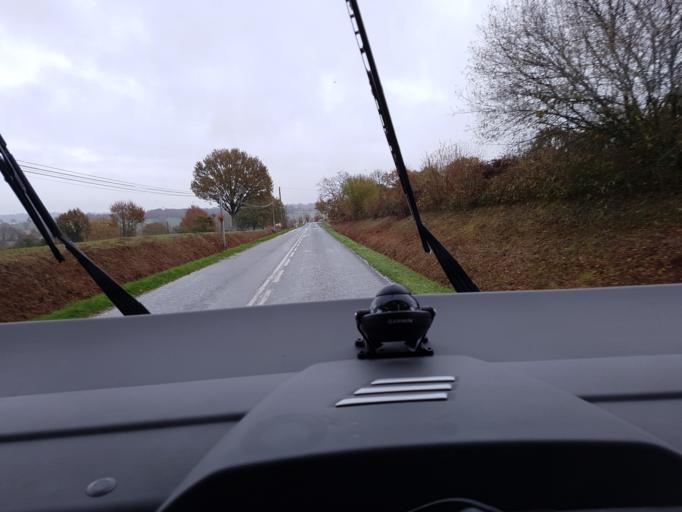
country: FR
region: Pays de la Loire
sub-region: Departement de la Mayenne
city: La Baconniere
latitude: 48.1884
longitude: -0.8808
